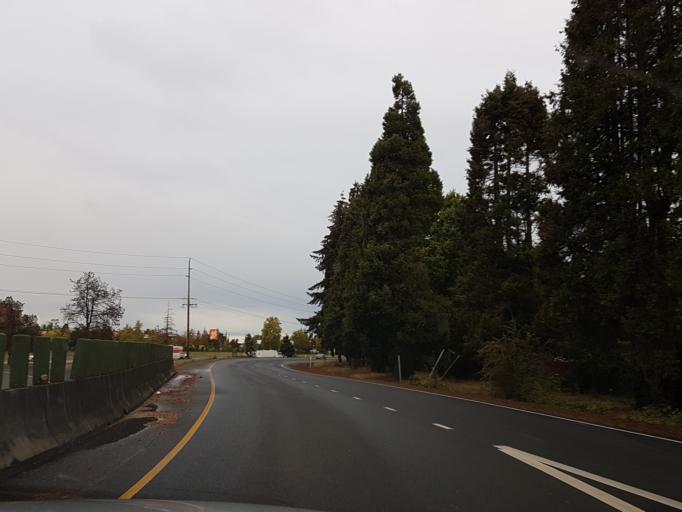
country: US
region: Oregon
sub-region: Linn County
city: Albany
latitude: 44.6293
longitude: -123.0640
